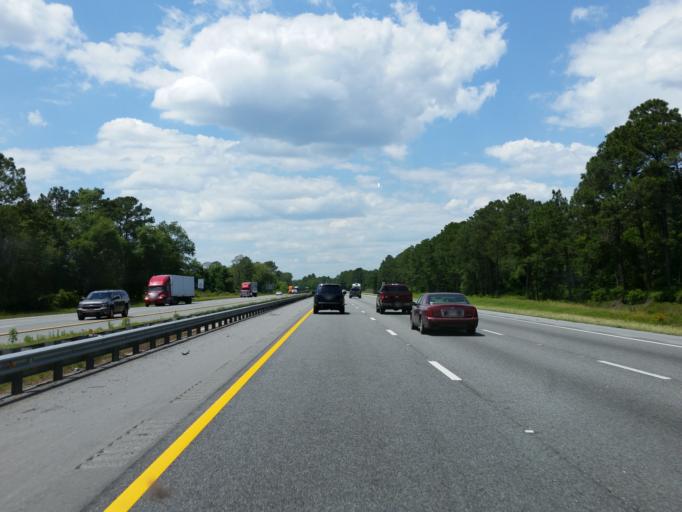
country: US
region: Georgia
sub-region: Echols County
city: Statenville
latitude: 30.6000
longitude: -83.1252
